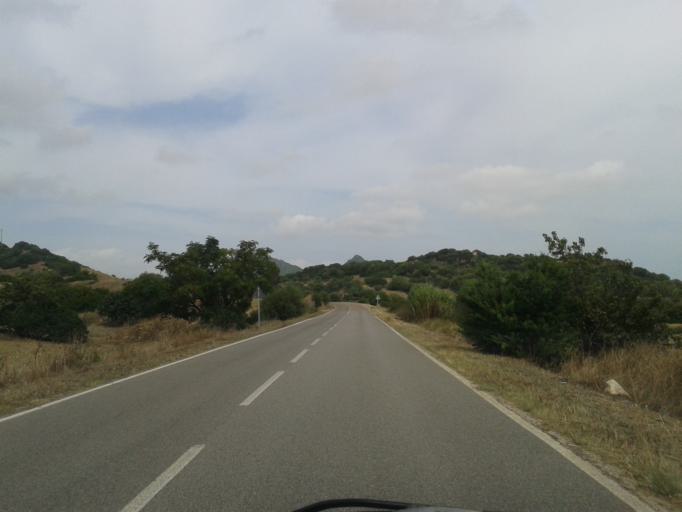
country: IT
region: Sardinia
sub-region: Provincia di Cagliari
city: Villasimius
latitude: 39.1894
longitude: 9.5582
